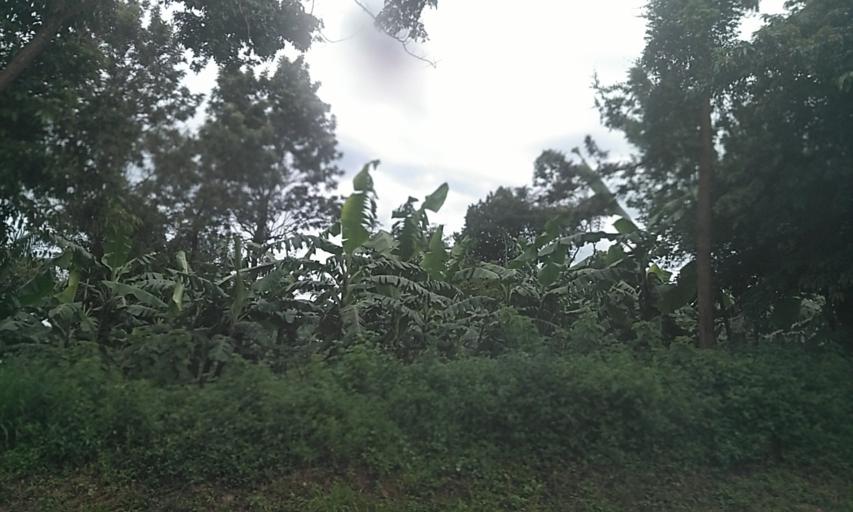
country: UG
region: Central Region
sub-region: Wakiso District
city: Bweyogerere
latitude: 0.3947
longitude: 32.6908
